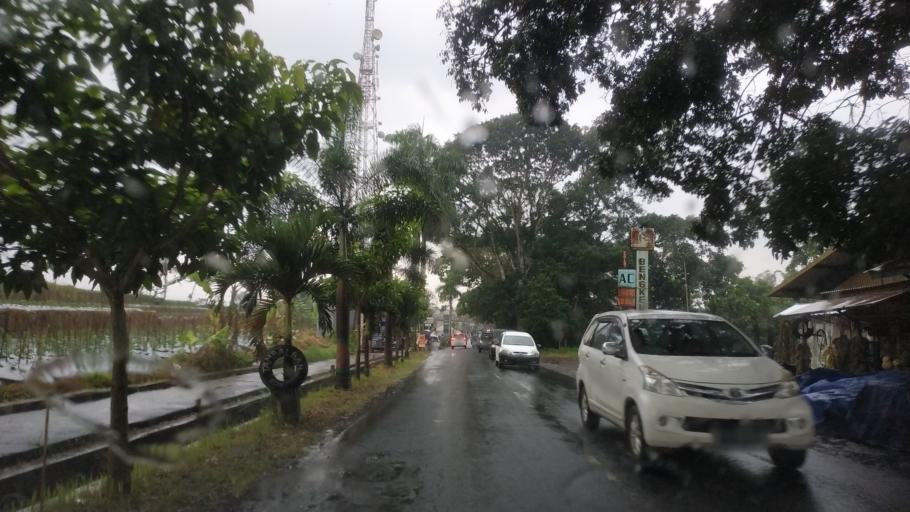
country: ID
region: Central Java
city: Magelang
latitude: -7.3148
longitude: 110.1680
